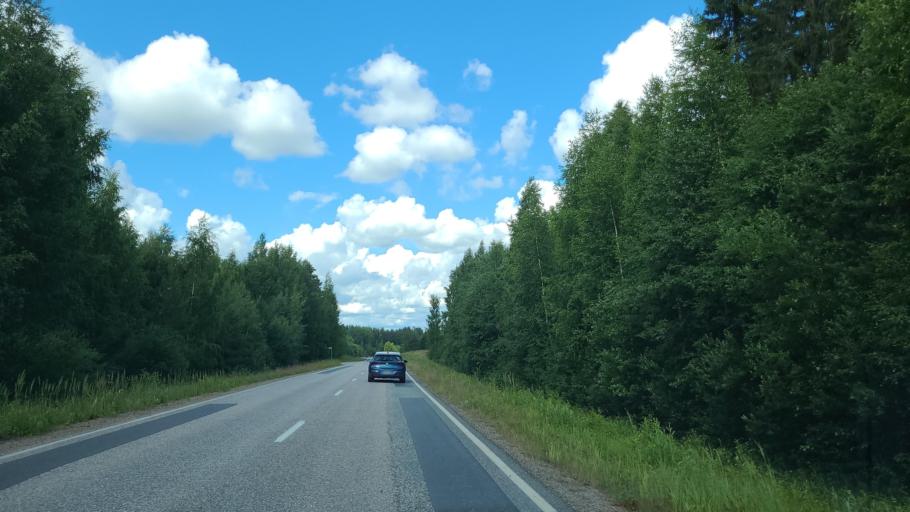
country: FI
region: Northern Savo
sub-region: Koillis-Savo
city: Kaavi
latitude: 62.9085
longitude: 28.7155
